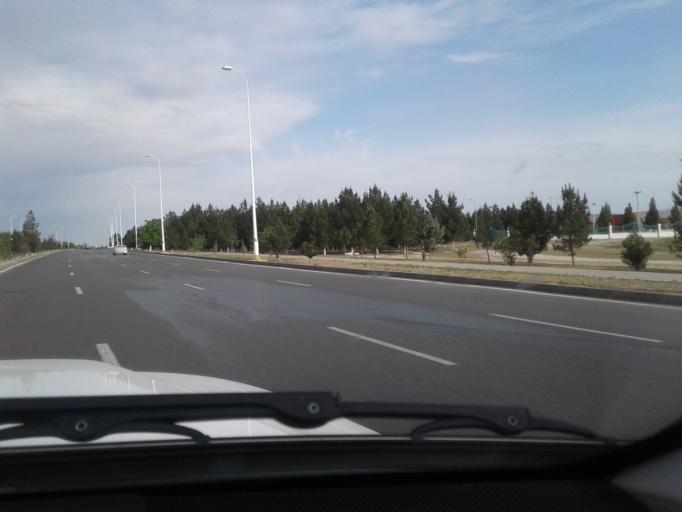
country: TM
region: Ahal
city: Abadan
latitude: 38.0081
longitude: 58.2834
